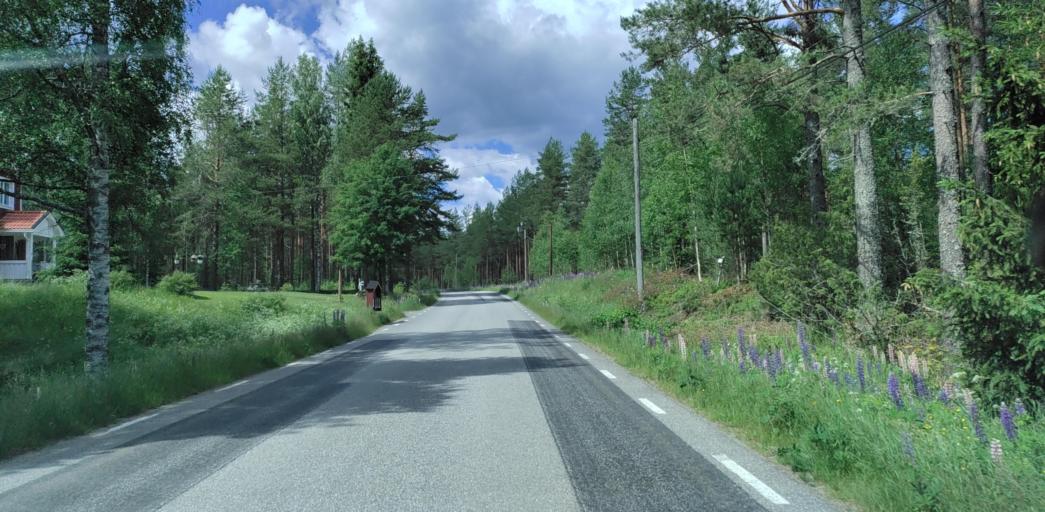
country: SE
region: Vaermland
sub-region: Hagfors Kommun
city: Ekshaerad
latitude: 60.0714
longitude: 13.5347
